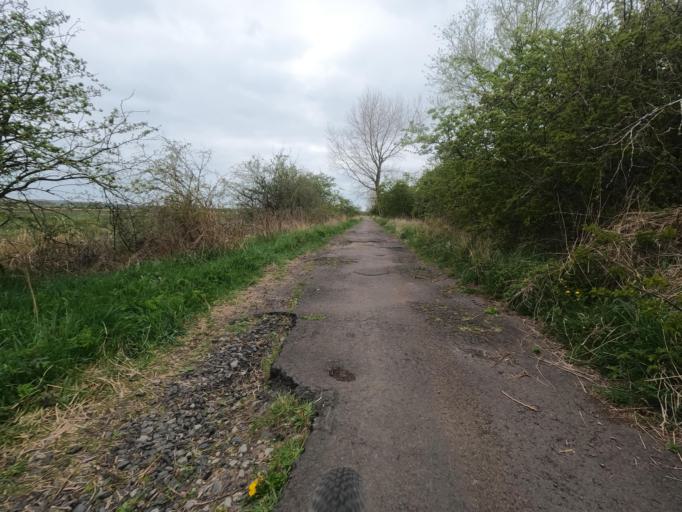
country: GB
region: England
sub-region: Newcastle upon Tyne
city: Dinnington
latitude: 55.0565
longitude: -1.7050
